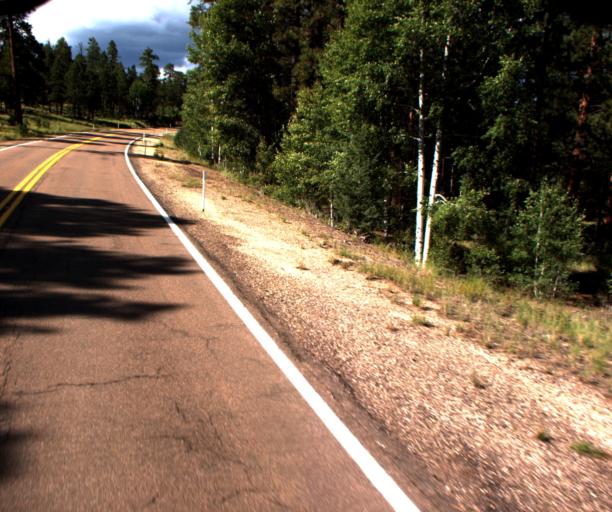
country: US
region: Arizona
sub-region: Apache County
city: Eagar
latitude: 34.0601
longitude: -109.4972
